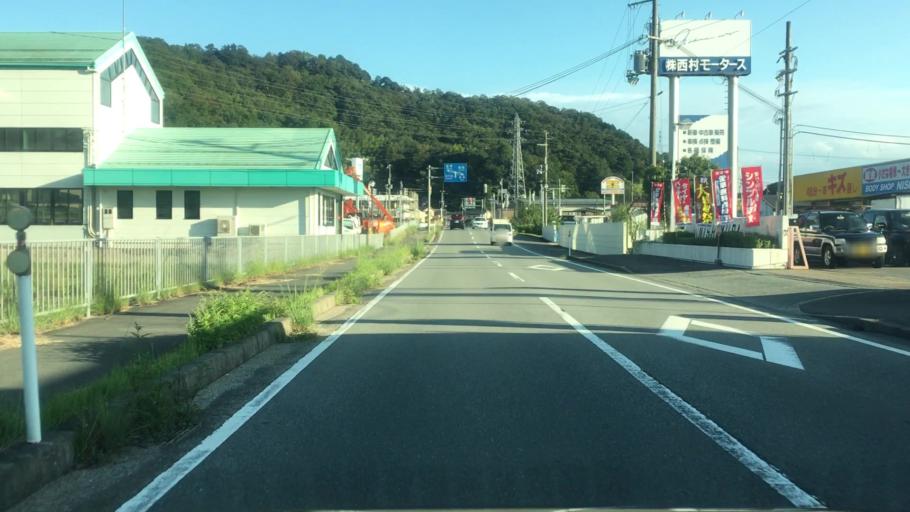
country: JP
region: Hyogo
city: Toyooka
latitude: 35.5599
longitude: 134.8238
